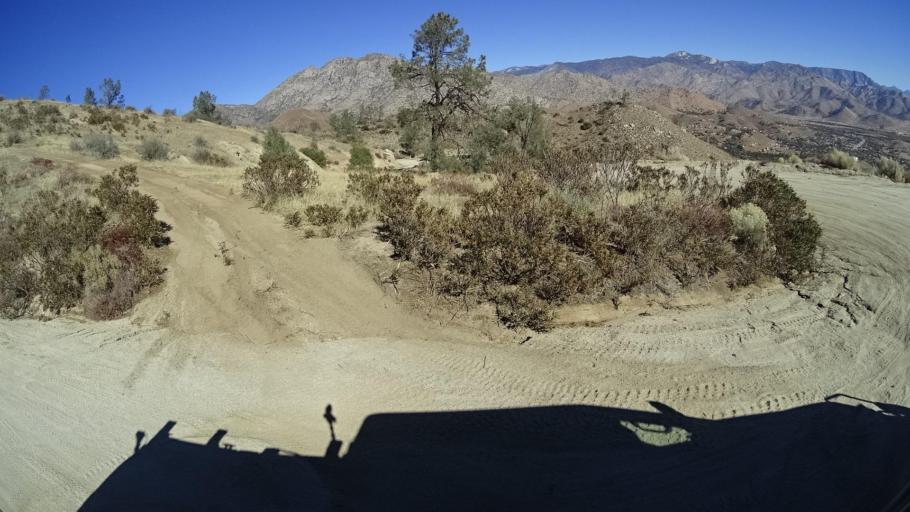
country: US
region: California
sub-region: Kern County
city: Wofford Heights
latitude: 35.7019
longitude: -118.4896
